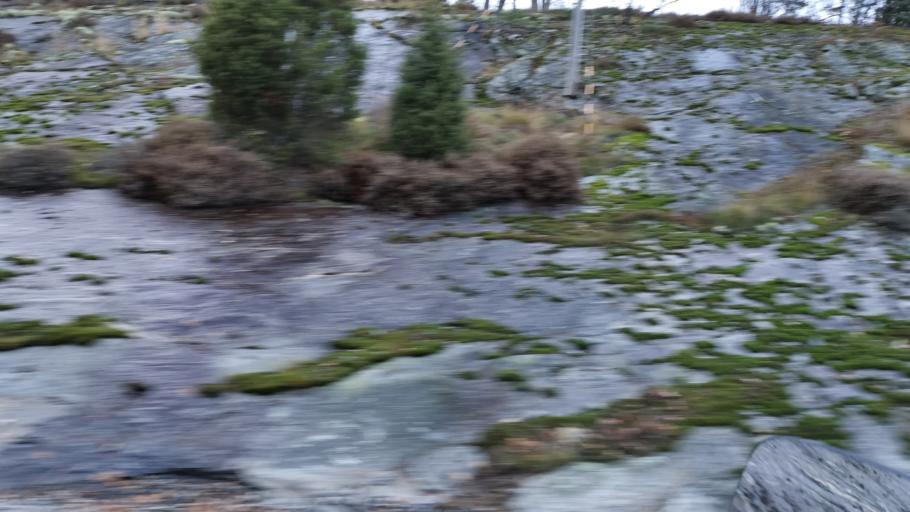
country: SE
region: Vaestra Goetaland
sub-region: Orust
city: Henan
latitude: 58.2561
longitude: 11.7266
